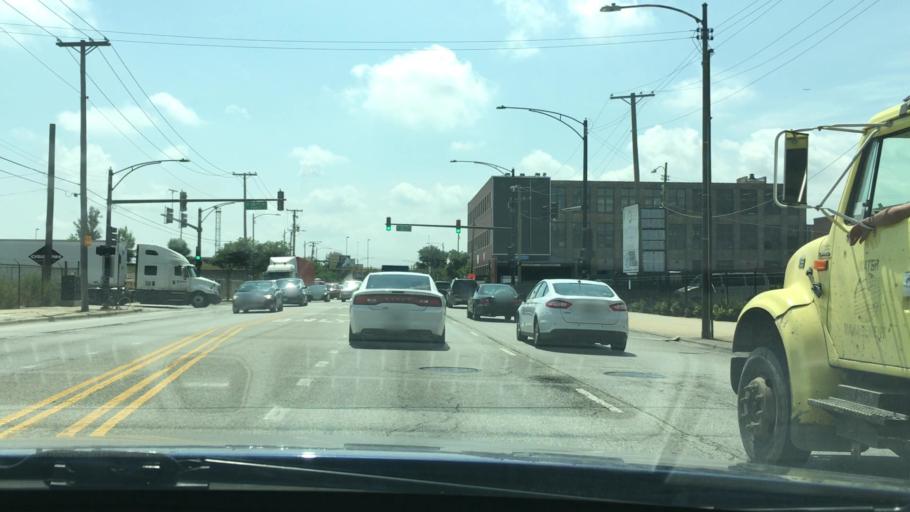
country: US
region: Illinois
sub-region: Cook County
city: Chicago
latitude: 41.8599
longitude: -87.6859
